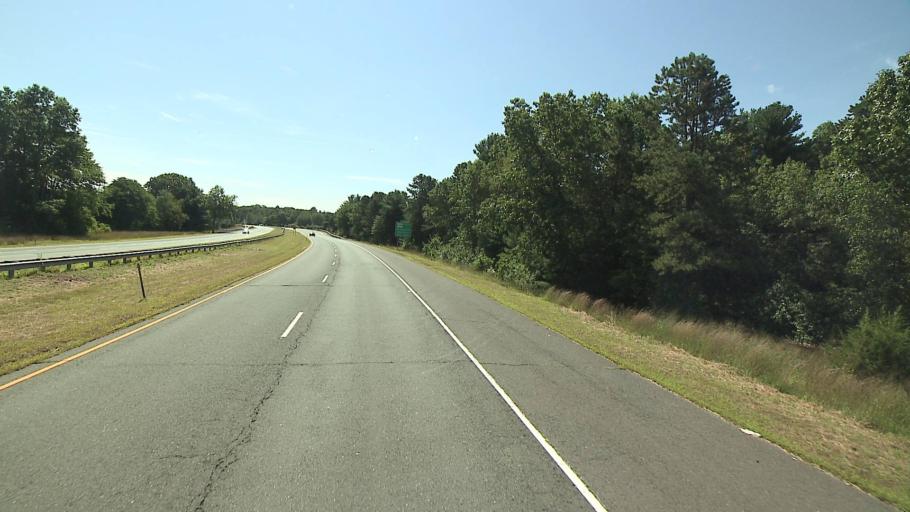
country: US
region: Connecticut
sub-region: Hartford County
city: Tariffville
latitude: 41.8848
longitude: -72.7473
